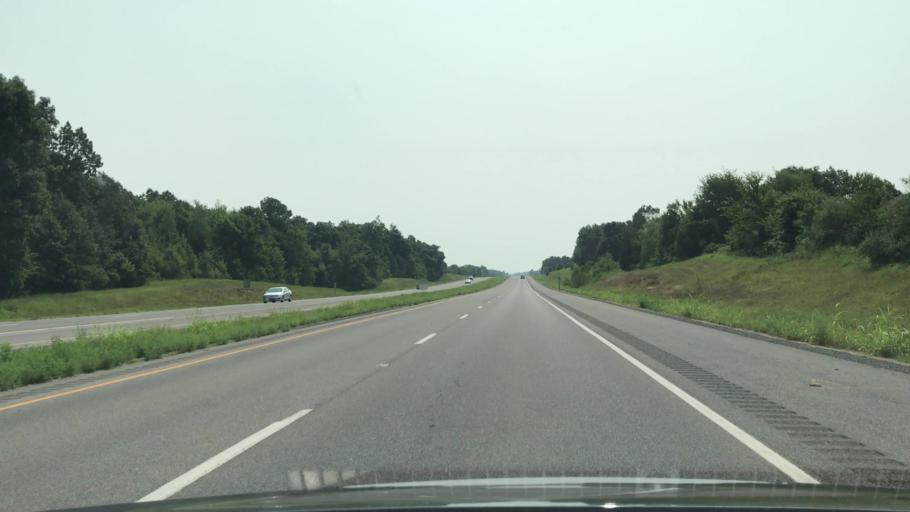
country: US
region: Kentucky
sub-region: Graves County
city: Mayfield
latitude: 36.6731
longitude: -88.5097
